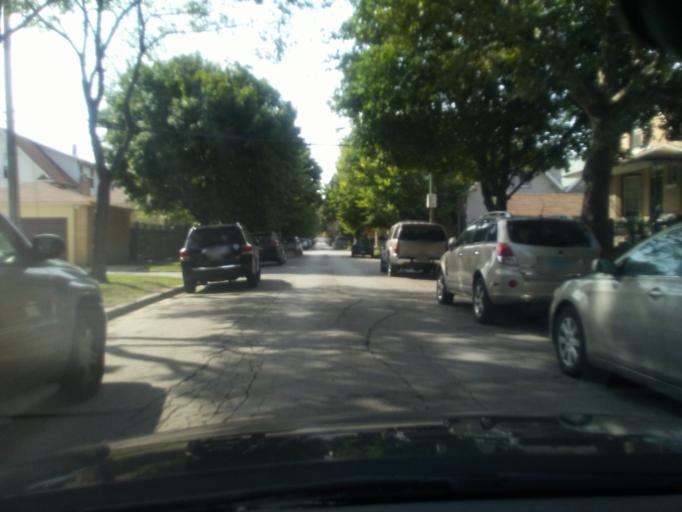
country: US
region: Illinois
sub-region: Cook County
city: Lincolnwood
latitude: 41.9358
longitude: -87.6944
